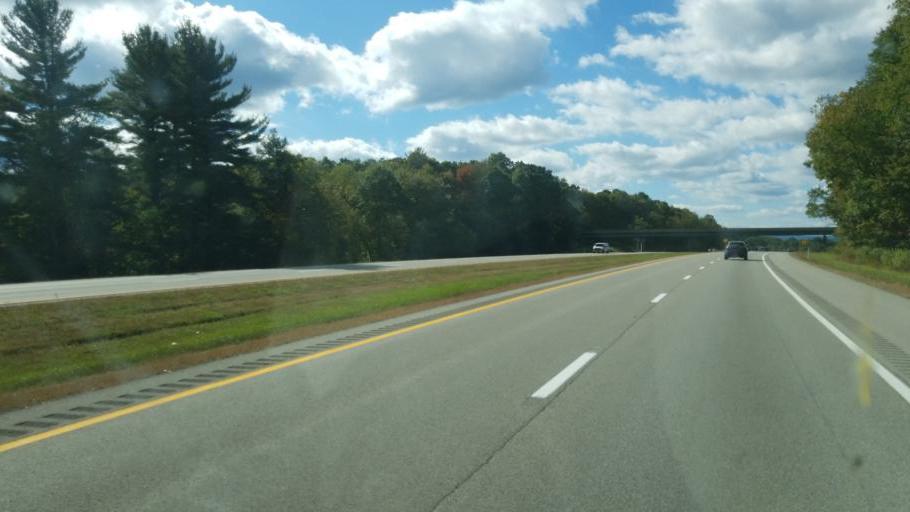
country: US
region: West Virginia
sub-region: Preston County
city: Terra Alta
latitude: 39.6573
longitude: -79.5707
